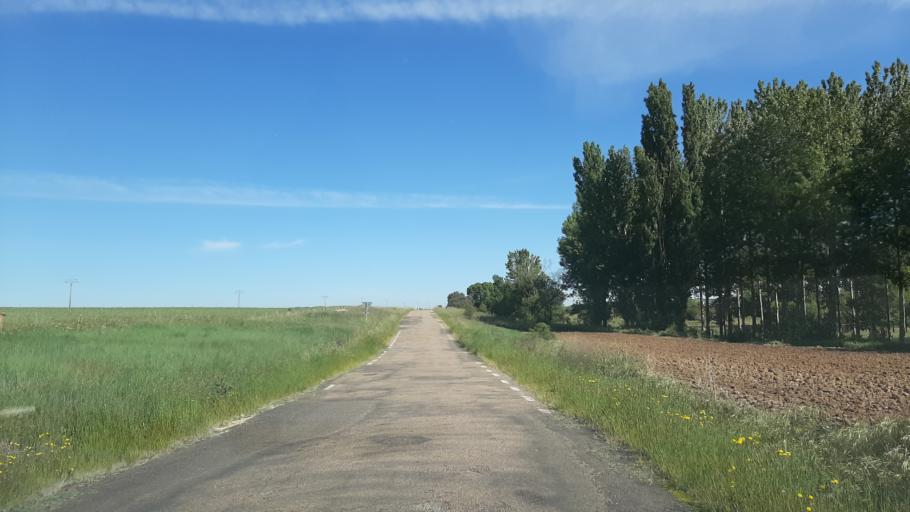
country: ES
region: Castille and Leon
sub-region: Provincia de Salamanca
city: Gajates
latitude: 40.7892
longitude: -5.3699
